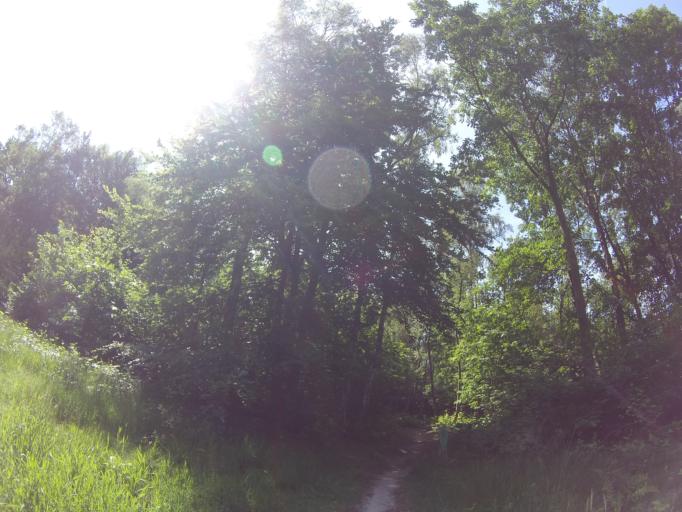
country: NL
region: Utrecht
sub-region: Gemeente Amersfoort
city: Amersfoort
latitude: 52.1432
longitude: 5.3558
